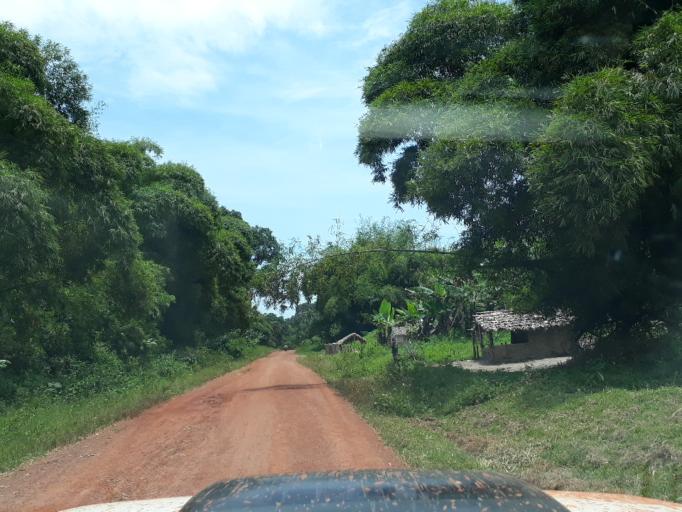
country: CD
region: Eastern Province
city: Buta
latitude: 2.6413
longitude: 24.8056
